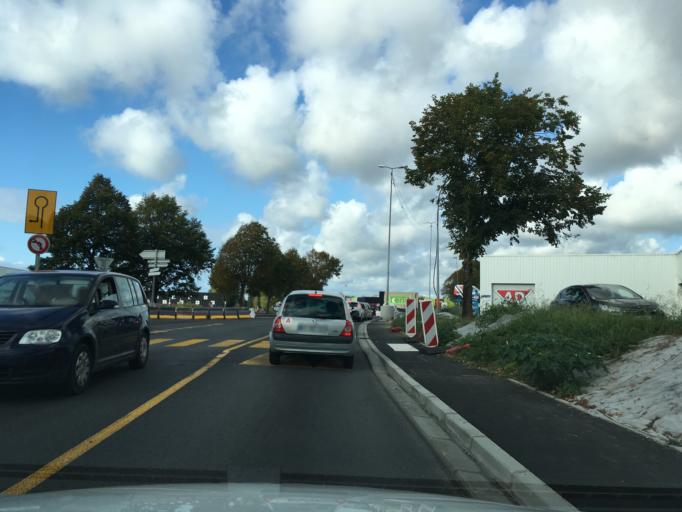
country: FR
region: Aquitaine
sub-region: Departement des Pyrenees-Atlantiques
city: Bayonne
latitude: 43.4924
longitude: -1.4955
